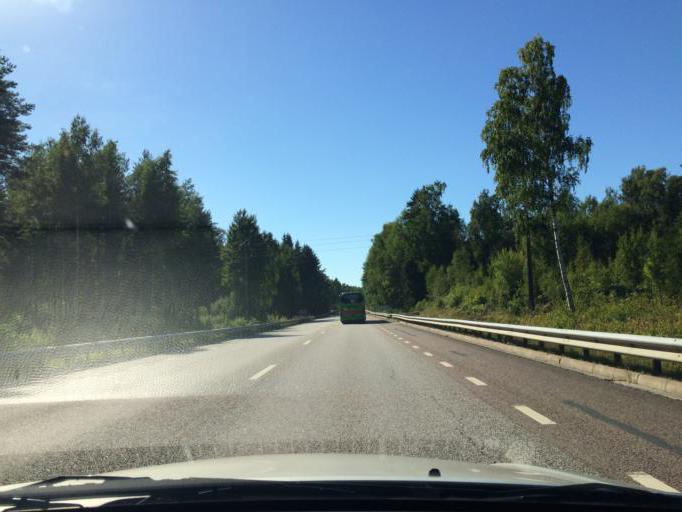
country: SE
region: Soedermanland
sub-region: Eskilstuna Kommun
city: Skogstorp
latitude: 59.3290
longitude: 16.4455
